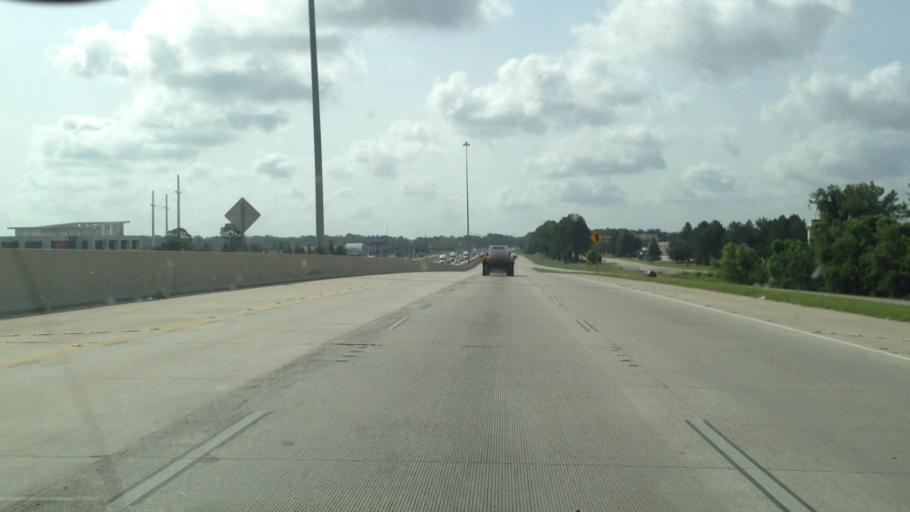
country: US
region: Louisiana
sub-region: East Baton Rouge Parish
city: Village Saint George
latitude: 30.3817
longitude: -91.0653
